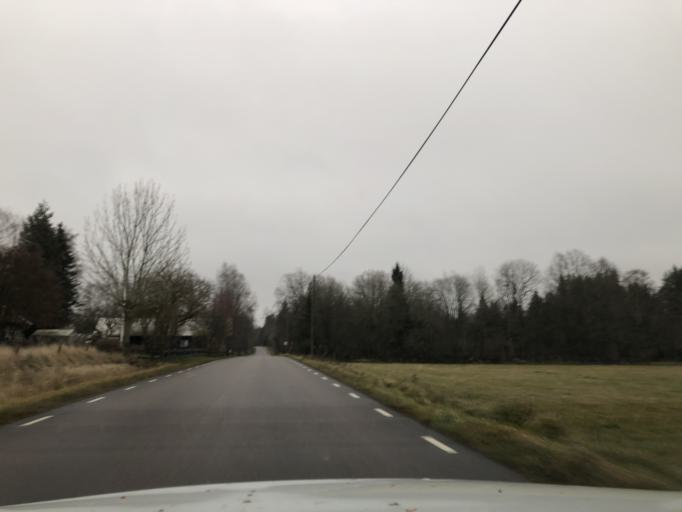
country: SE
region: Vaestra Goetaland
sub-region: Ulricehamns Kommun
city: Ulricehamn
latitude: 57.8413
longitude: 13.3775
